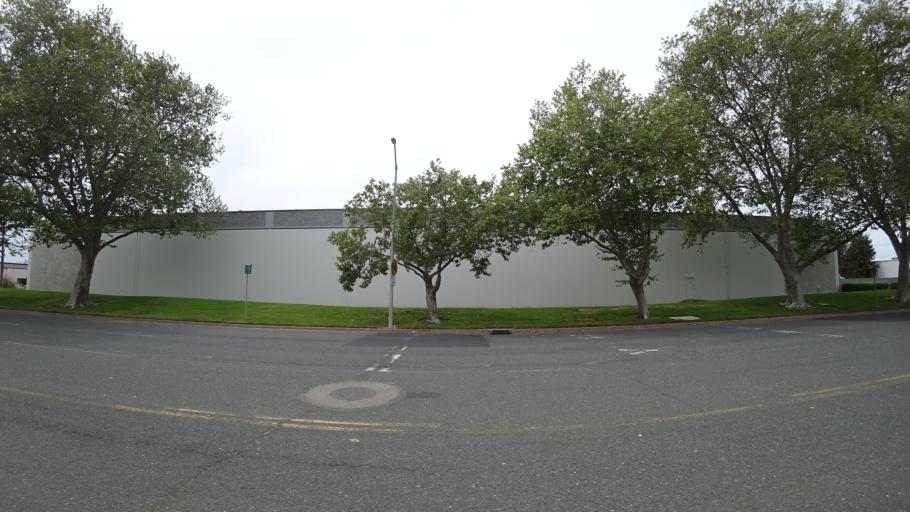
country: US
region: California
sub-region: Alameda County
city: San Lorenzo
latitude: 37.6491
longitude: -122.1376
